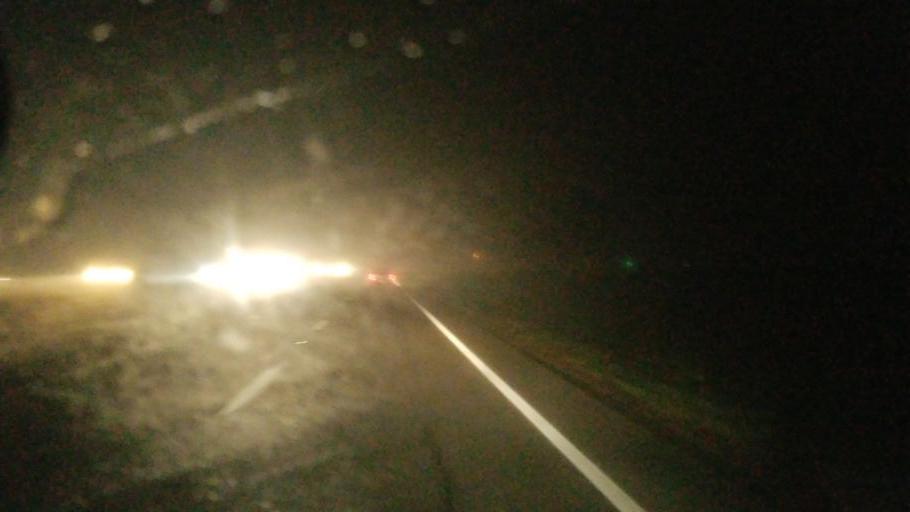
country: US
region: Ohio
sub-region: Pickaway County
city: South Bloomfield
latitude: 39.7468
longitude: -82.9889
